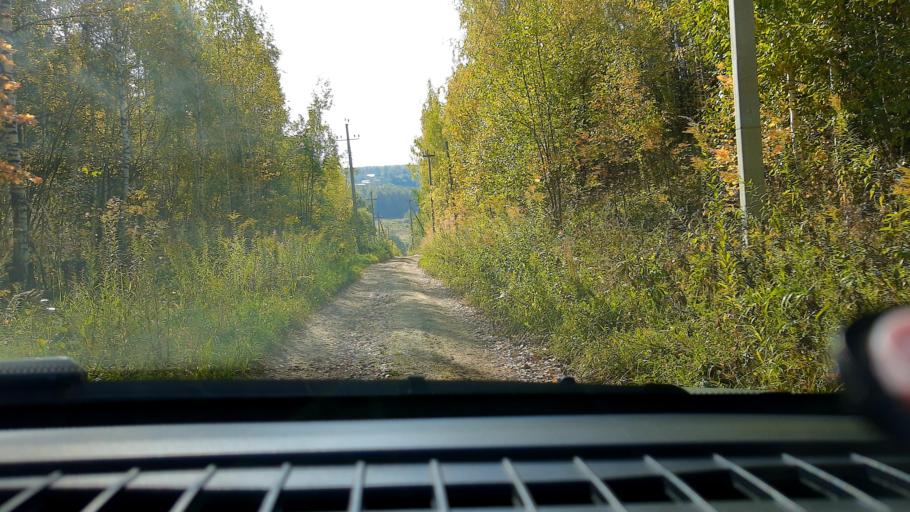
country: RU
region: Nizjnij Novgorod
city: Afonino
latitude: 56.2415
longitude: 44.0588
